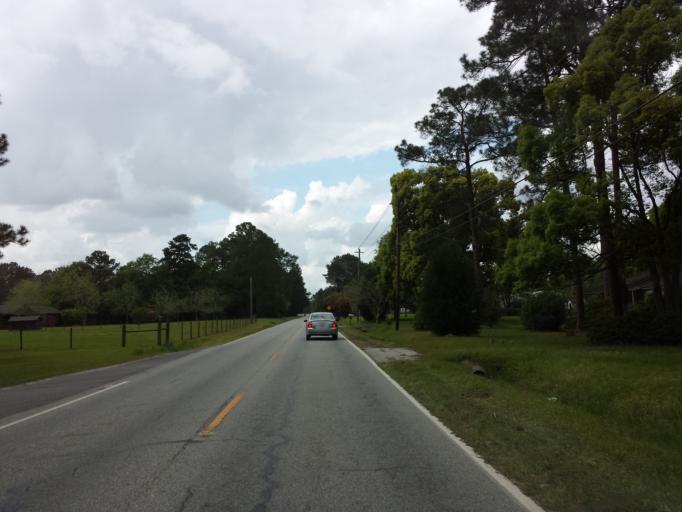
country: US
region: Georgia
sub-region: Lowndes County
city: Hahira
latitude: 31.0128
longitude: -83.3772
